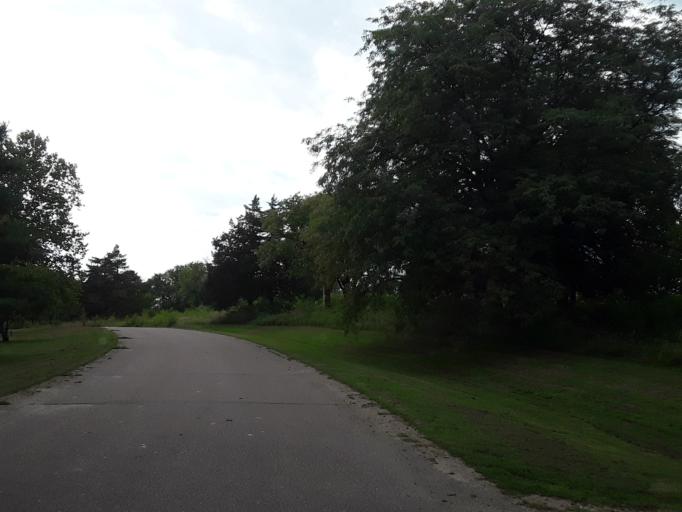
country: US
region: Nebraska
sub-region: Saunders County
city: Ashland
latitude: 41.1024
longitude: -96.4368
